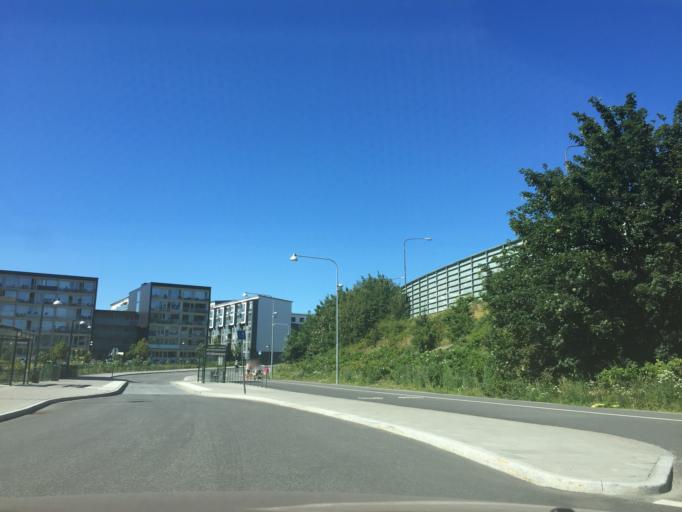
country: SE
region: Stockholm
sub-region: Stockholms Kommun
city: OEstermalm
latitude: 59.3081
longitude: 18.1069
